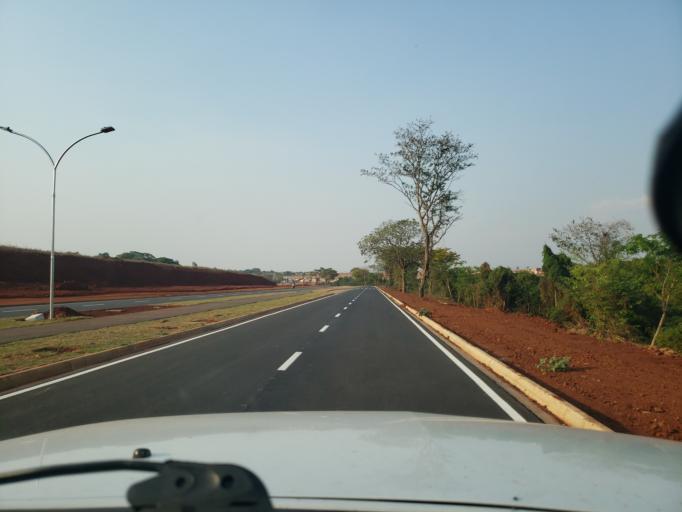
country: BR
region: Sao Paulo
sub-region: Moji-Guacu
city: Mogi-Gaucu
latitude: -22.3215
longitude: -46.9474
